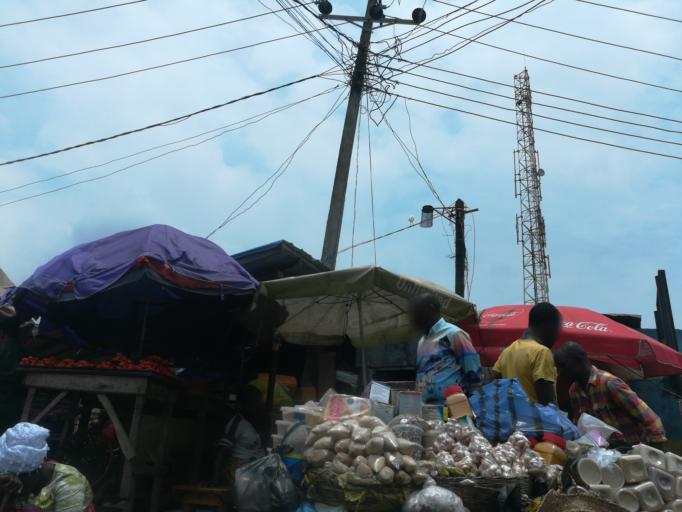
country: NG
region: Lagos
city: Lagos
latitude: 6.4513
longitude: 3.4006
